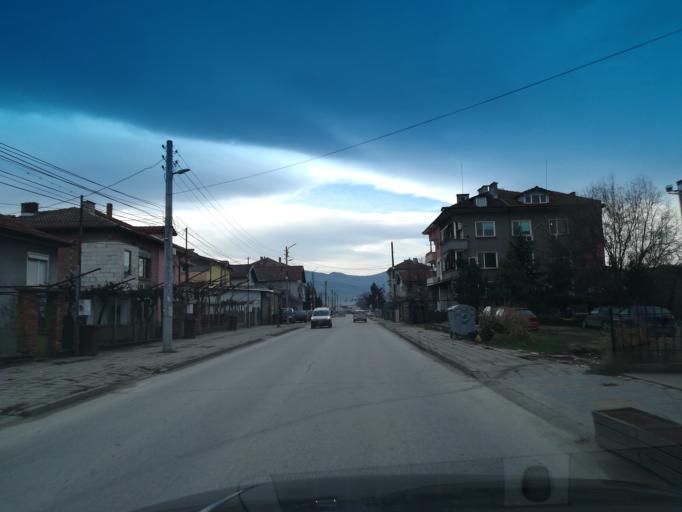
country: BG
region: Plovdiv
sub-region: Obshtina Plovdiv
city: Plovdiv
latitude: 42.0979
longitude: 24.6995
